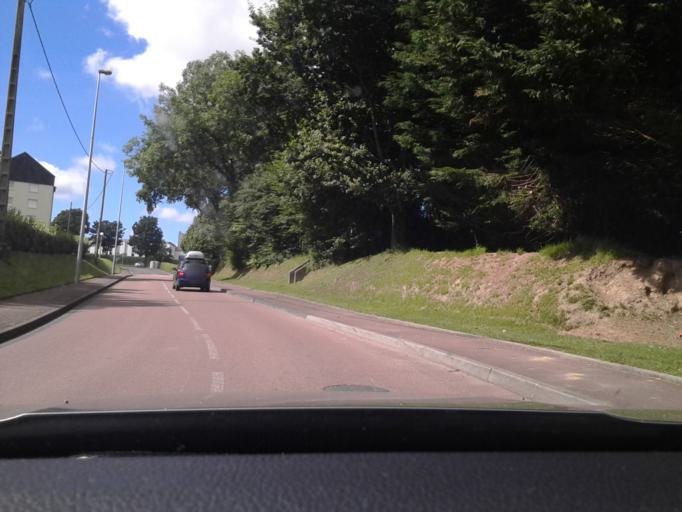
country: FR
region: Lower Normandy
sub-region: Departement de la Manche
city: Coutances
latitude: 49.0561
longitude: -1.4283
